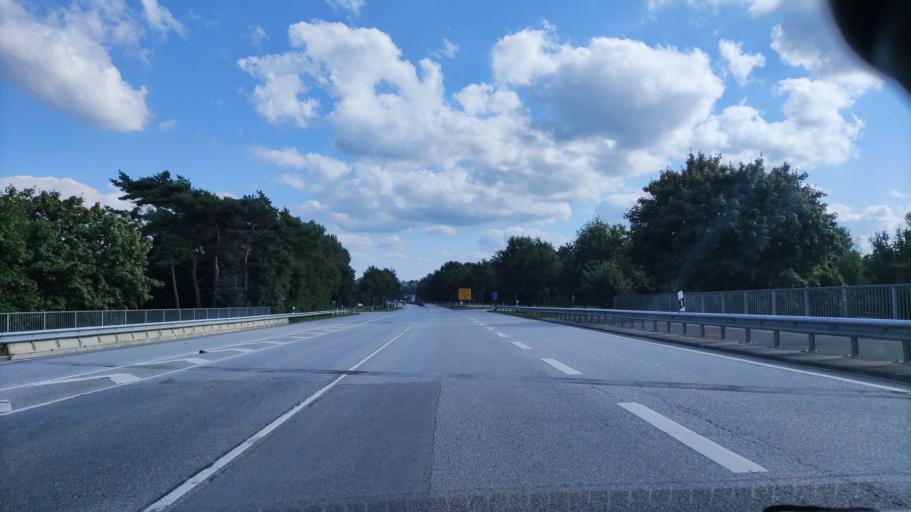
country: DE
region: Schleswig-Holstein
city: Fockbek
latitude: 54.3104
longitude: 9.6272
